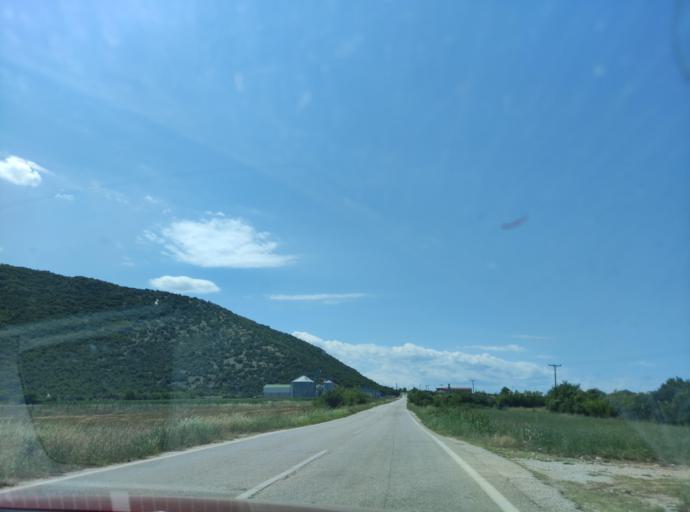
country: GR
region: East Macedonia and Thrace
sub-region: Nomos Kavalas
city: Palaiochori
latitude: 40.9699
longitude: 24.1702
